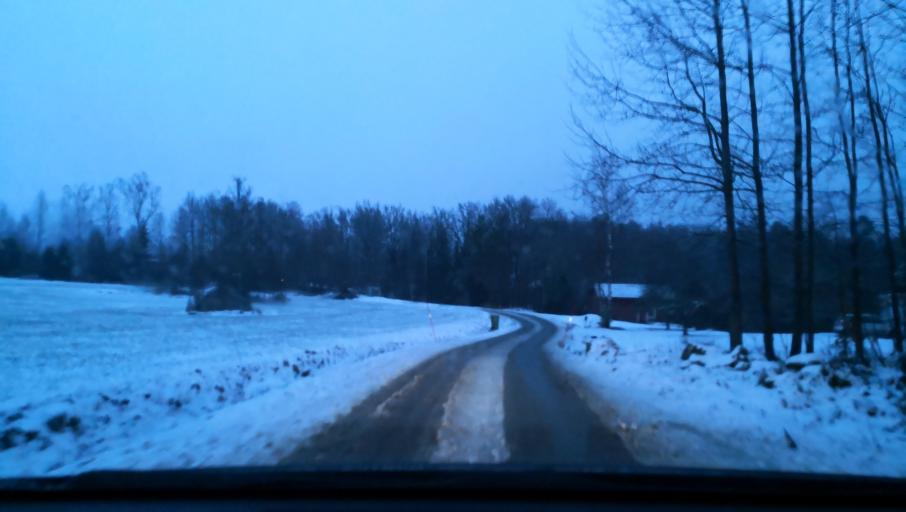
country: SE
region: Soedermanland
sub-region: Eskilstuna Kommun
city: Kvicksund
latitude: 59.3728
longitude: 16.2841
